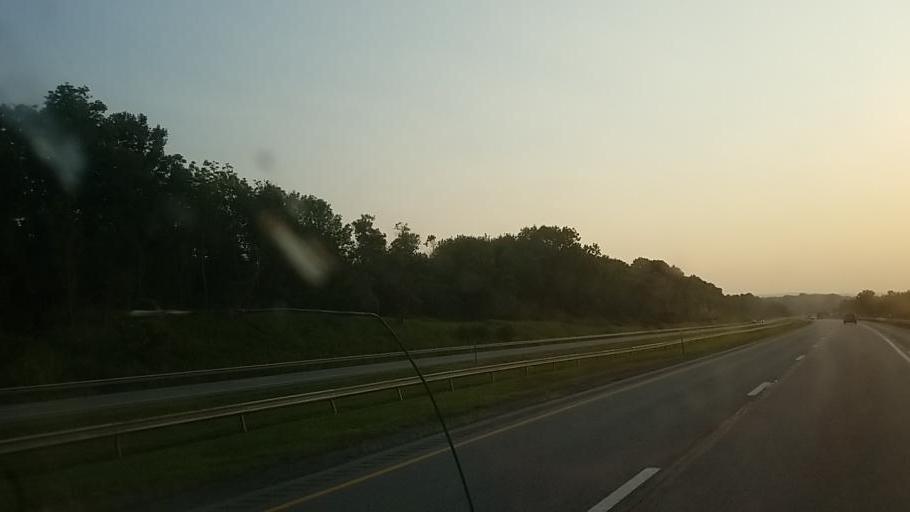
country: US
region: New York
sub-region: Herkimer County
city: Herkimer
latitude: 43.0146
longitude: -74.9626
